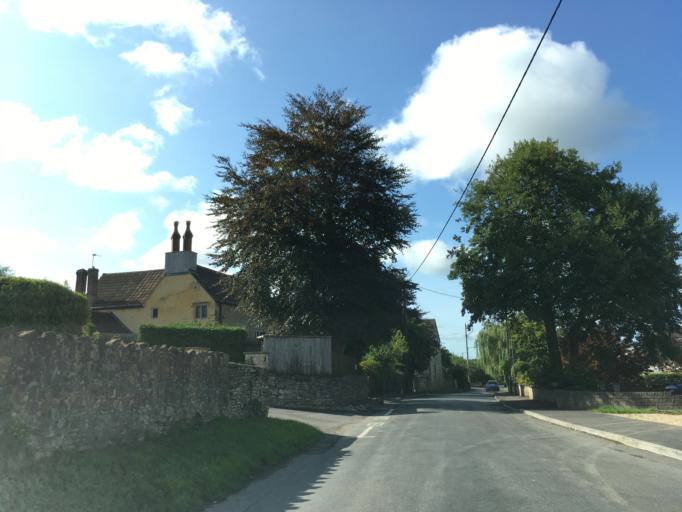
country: GB
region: England
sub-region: South Gloucestershire
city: Horton
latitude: 51.5313
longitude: -2.3576
